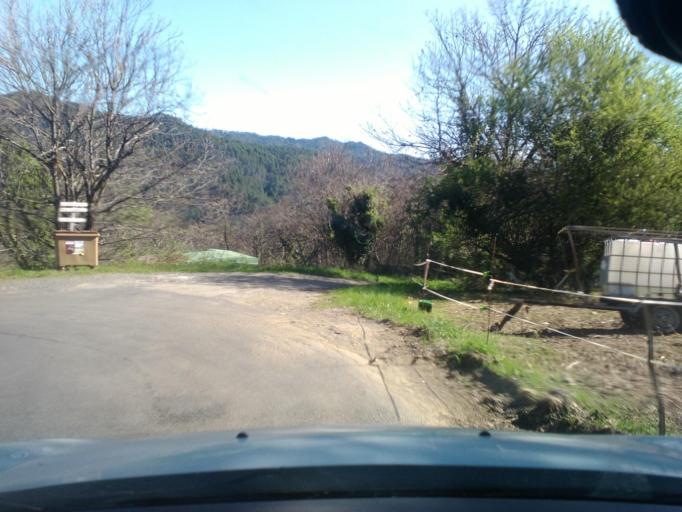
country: FR
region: Languedoc-Roussillon
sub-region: Departement du Gard
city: Saint-Jean-du-Gard
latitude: 44.1591
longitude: 3.7652
